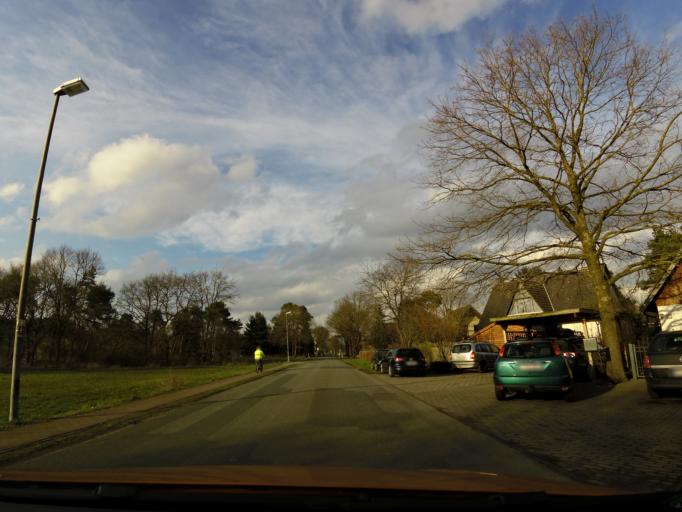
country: DE
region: Lower Saxony
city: Grethem
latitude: 52.7007
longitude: 9.4977
